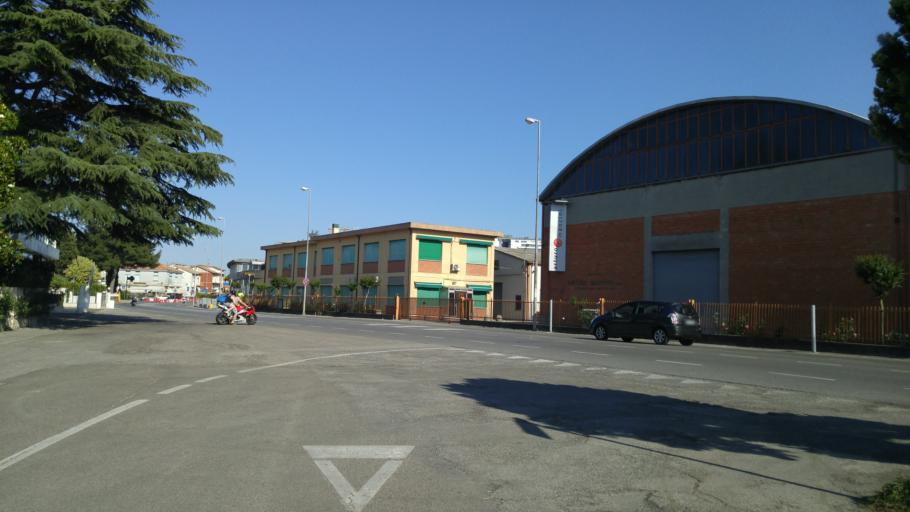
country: IT
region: The Marches
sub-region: Provincia di Pesaro e Urbino
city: Pesaro
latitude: 43.9066
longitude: 12.8859
